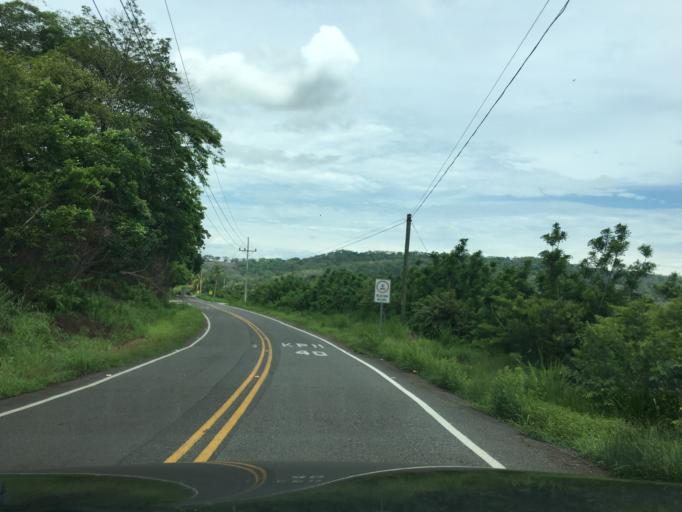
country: CR
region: Puntarenas
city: Esparza
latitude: 9.9329
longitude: -84.6936
